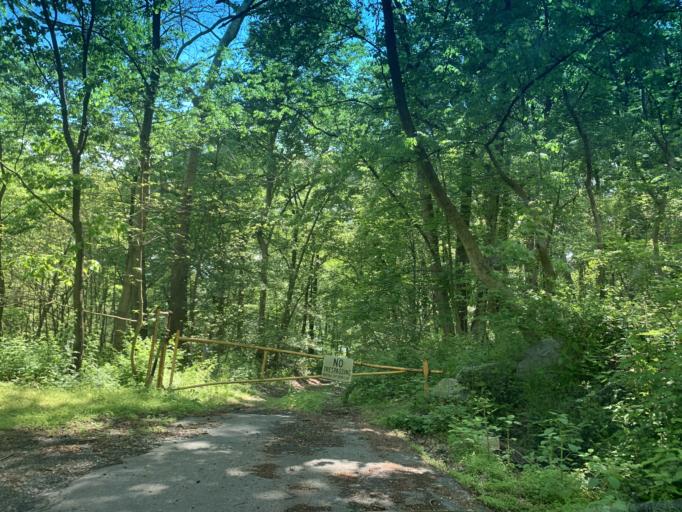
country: US
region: Maryland
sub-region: Cecil County
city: Rising Sun
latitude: 39.7025
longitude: -76.2103
